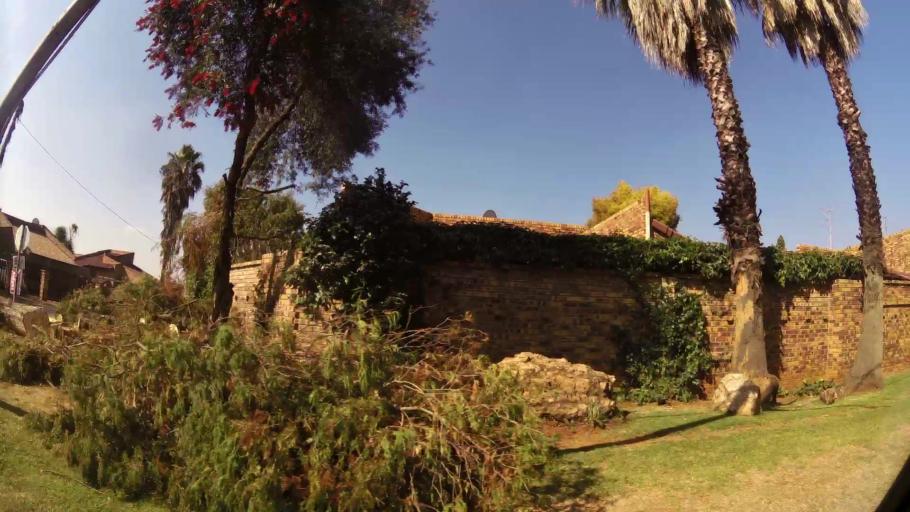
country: ZA
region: Gauteng
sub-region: Ekurhuleni Metropolitan Municipality
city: Boksburg
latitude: -26.1819
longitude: 28.2770
